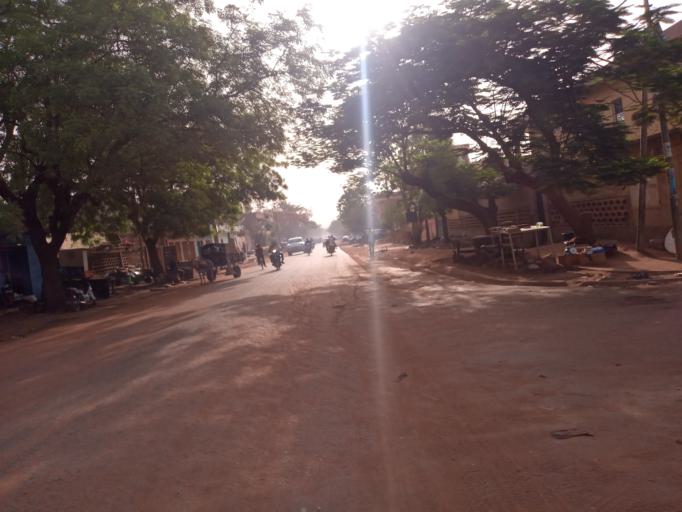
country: ML
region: Bamako
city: Bamako
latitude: 12.6650
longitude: -7.9738
